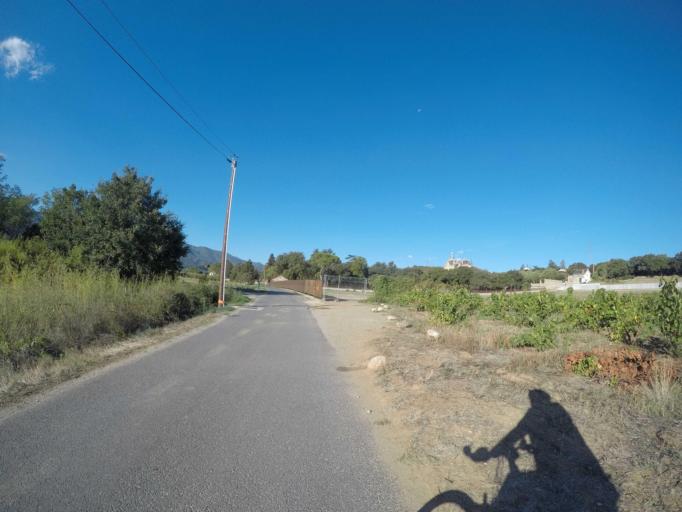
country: FR
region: Languedoc-Roussillon
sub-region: Departement des Pyrenees-Orientales
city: Sant Joan de Pladecorts
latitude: 42.5128
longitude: 2.7700
